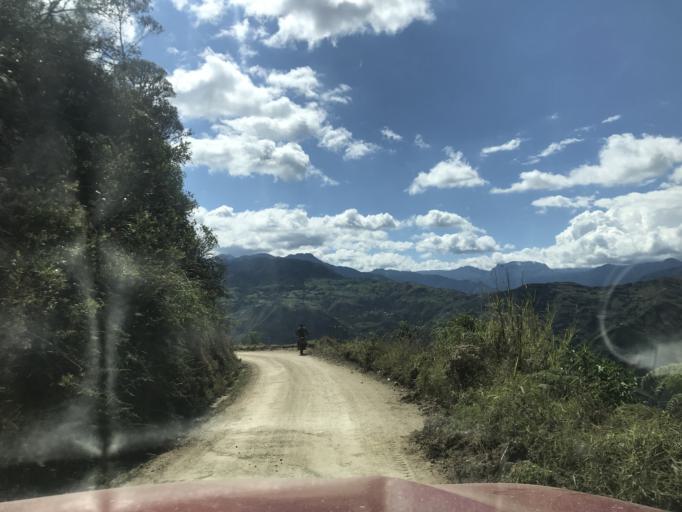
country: PE
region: Cajamarca
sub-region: Provincia de Chota
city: Querocoto
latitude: -6.3335
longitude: -79.0728
